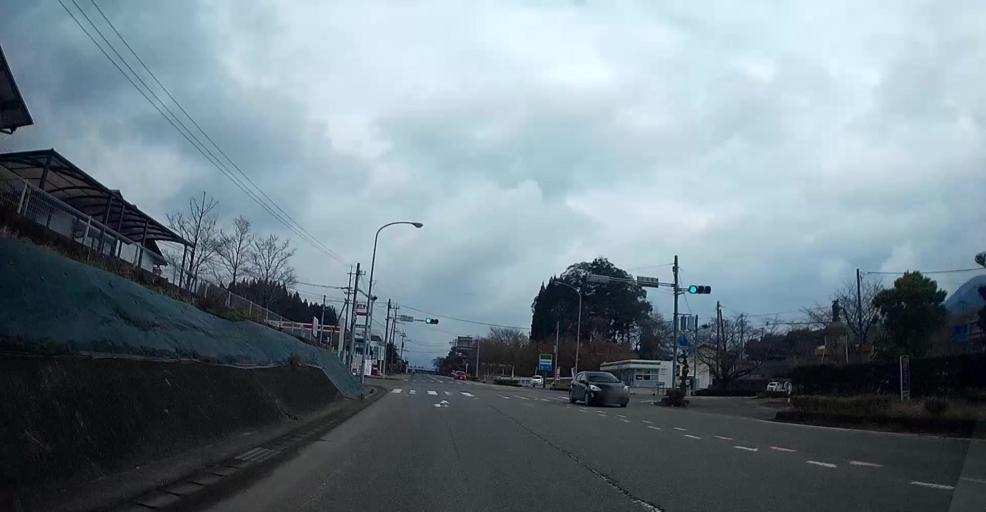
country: JP
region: Kumamoto
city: Matsubase
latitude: 32.6223
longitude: 130.8733
